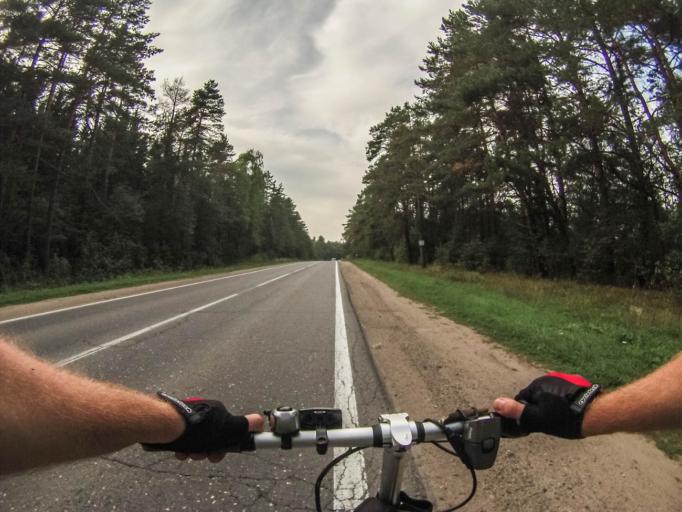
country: RU
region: Jaroslavl
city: Uglich
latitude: 57.4854
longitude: 38.3612
